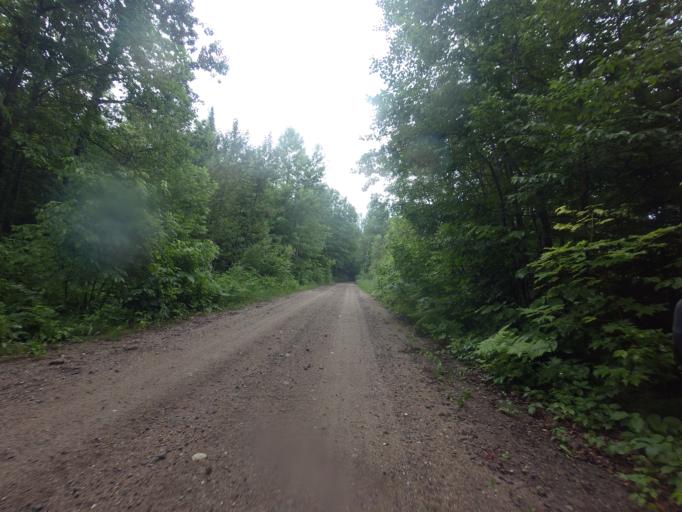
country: CA
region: Quebec
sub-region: Outaouais
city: Maniwaki
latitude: 46.3176
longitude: -76.0070
